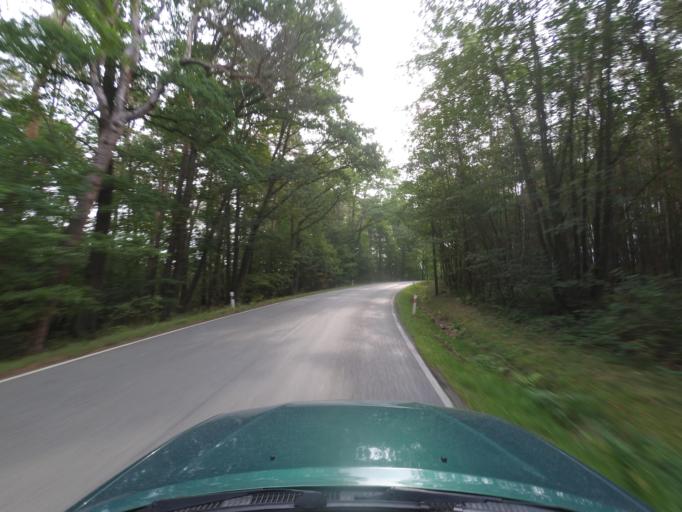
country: CZ
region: Plzensky
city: Hostoun
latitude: 49.5667
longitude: 12.8034
